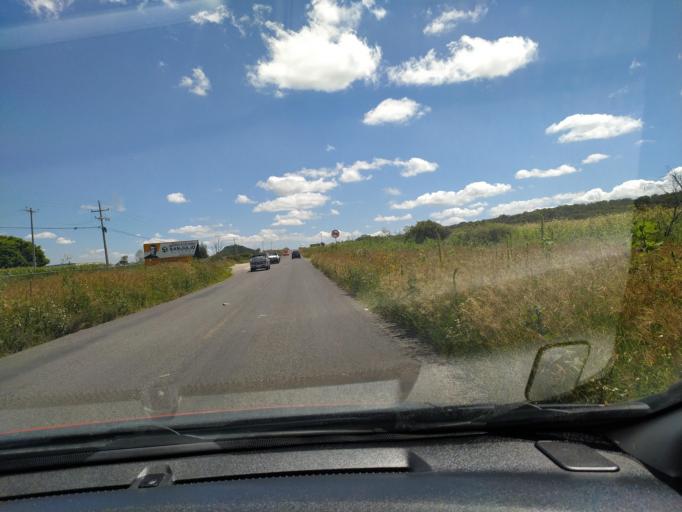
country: MX
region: Jalisco
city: San Julian
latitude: 21.0070
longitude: -102.1316
